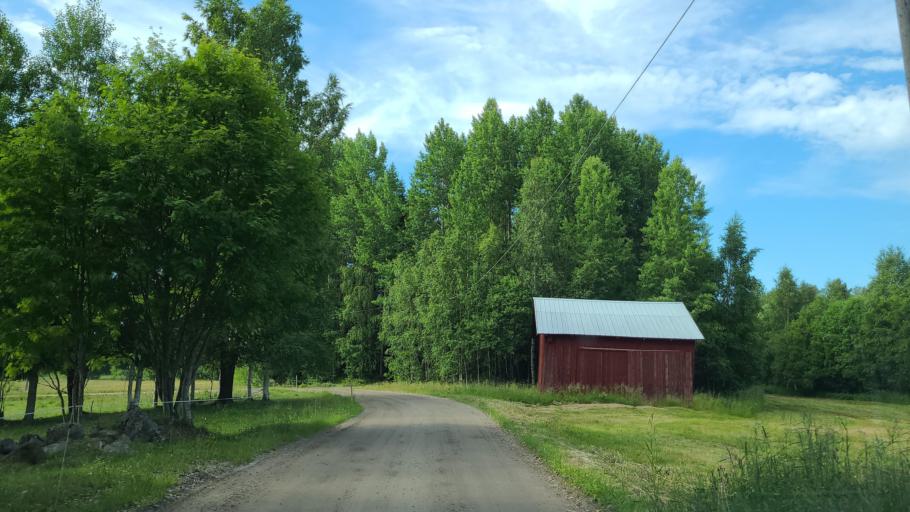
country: SE
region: Vaesterbotten
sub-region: Robertsfors Kommun
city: Robertsfors
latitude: 64.1563
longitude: 20.9234
